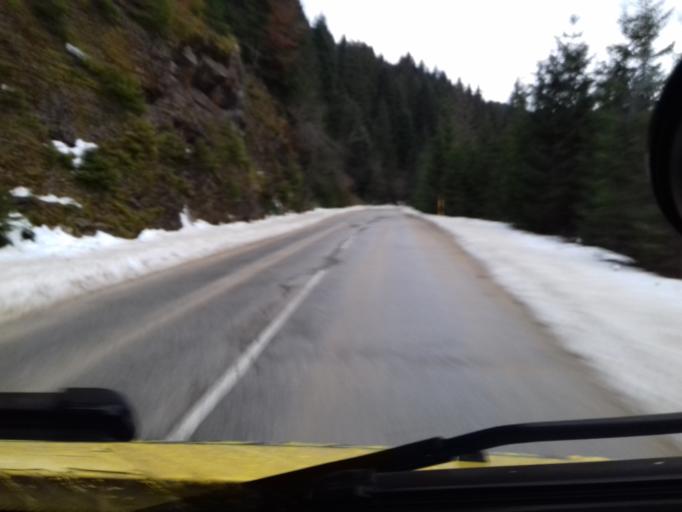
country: BA
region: Federation of Bosnia and Herzegovina
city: Turbe
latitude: 44.3157
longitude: 17.5035
